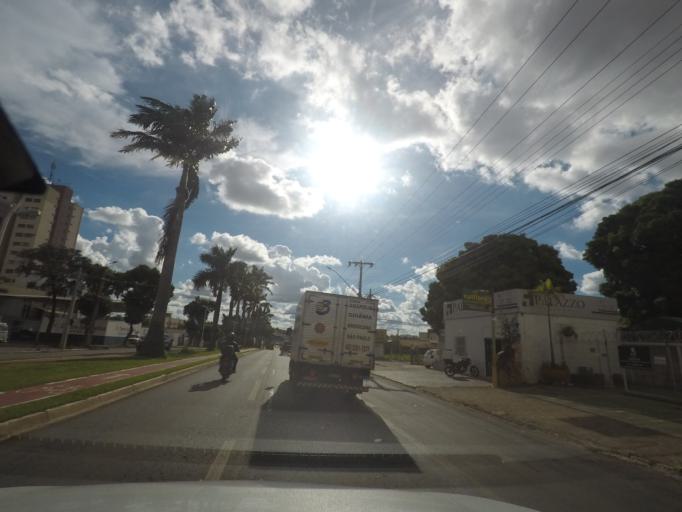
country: BR
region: Goias
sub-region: Goiania
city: Goiania
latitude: -16.7173
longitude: -49.2914
